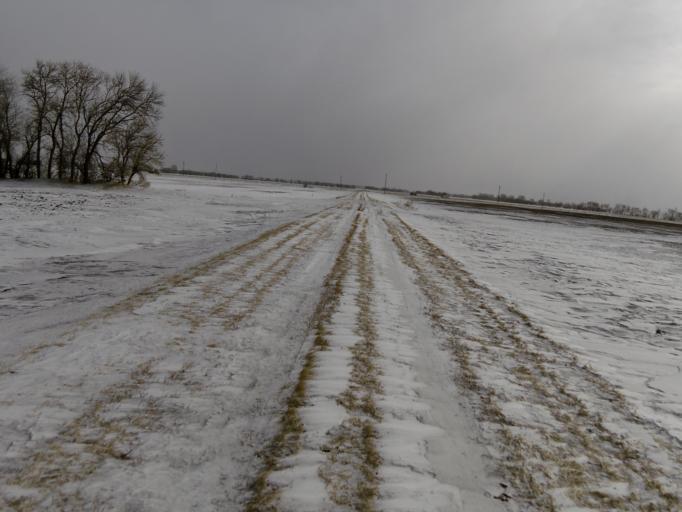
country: US
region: North Dakota
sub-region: Walsh County
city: Grafton
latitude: 48.3976
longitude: -97.1953
